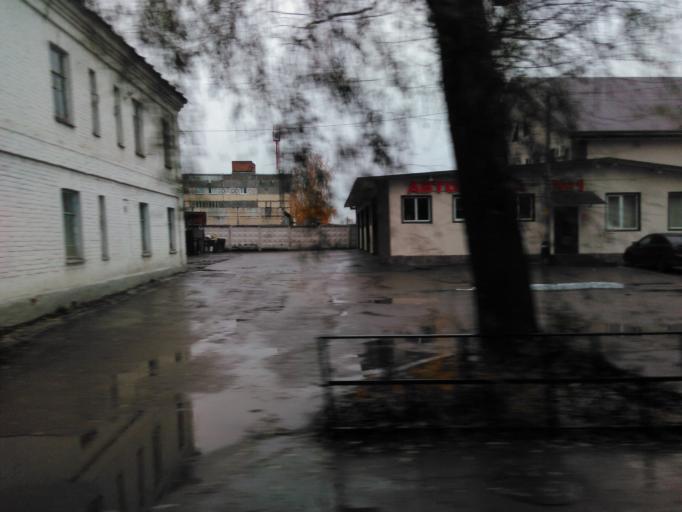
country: RU
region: Tatarstan
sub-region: Gorod Kazan'
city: Kazan
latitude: 55.7994
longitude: 49.0634
